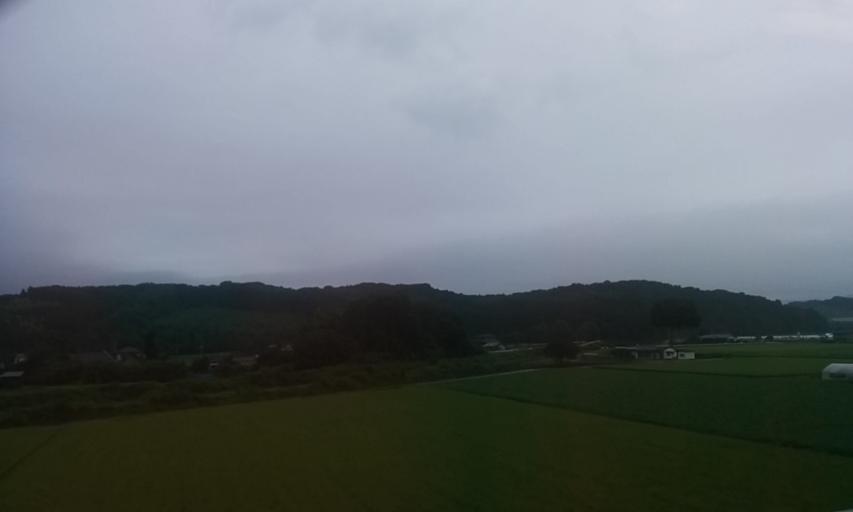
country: JP
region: Tochigi
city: Utsunomiya-shi
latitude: 36.6152
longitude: 139.9076
